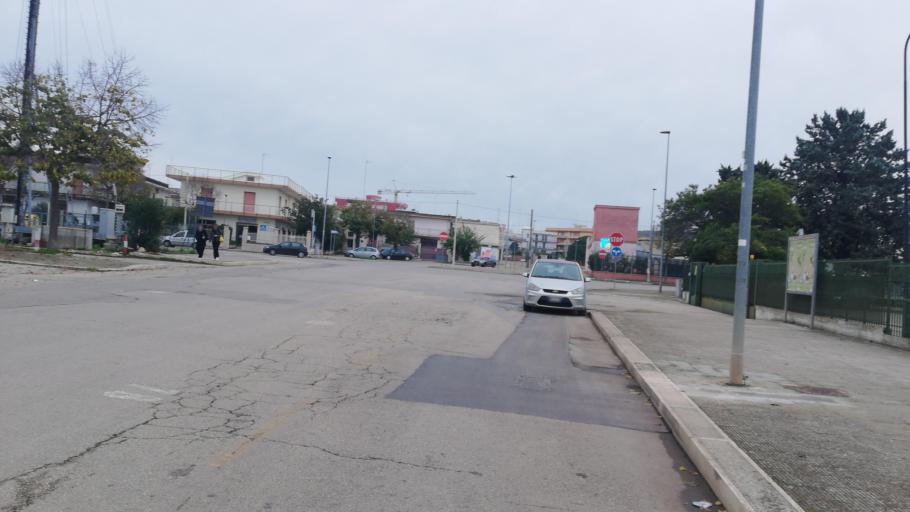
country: IT
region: Apulia
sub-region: Provincia di Bari
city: Bitonto
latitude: 41.1154
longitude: 16.6831
